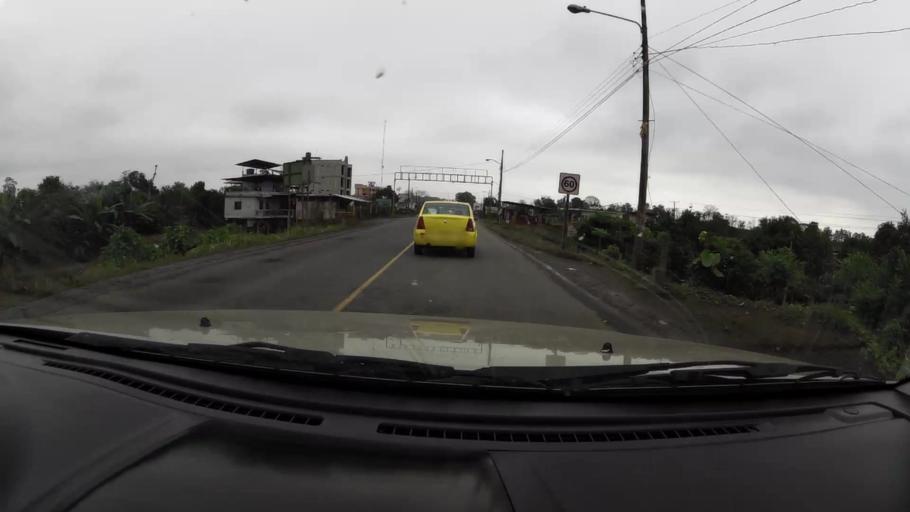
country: EC
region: Guayas
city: Balao
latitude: -3.0764
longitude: -79.7543
